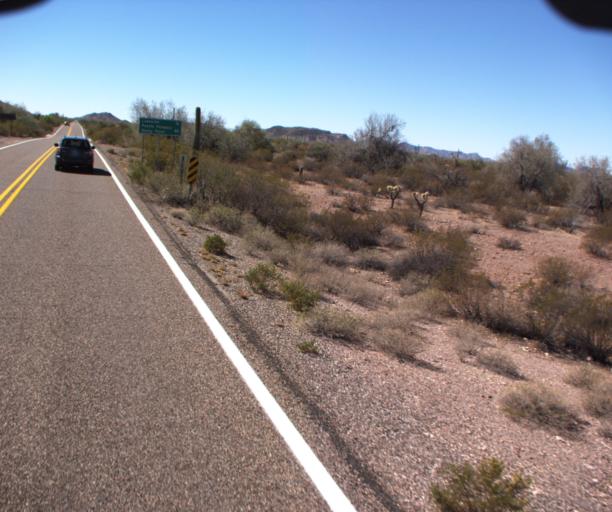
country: US
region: Arizona
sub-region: Pima County
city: Ajo
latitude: 32.1238
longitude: -112.7684
